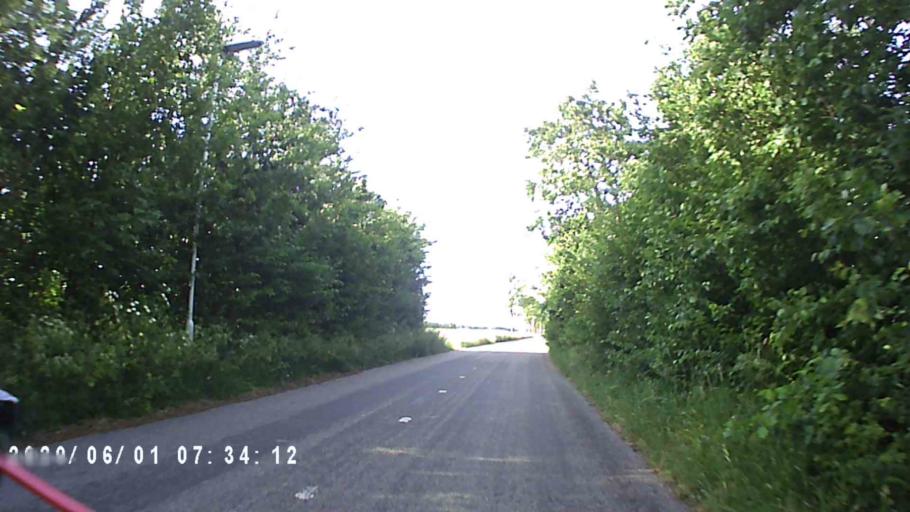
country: NL
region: Friesland
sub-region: Gemeente Dongeradeel
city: Dokkum
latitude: 53.3104
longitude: 5.9942
